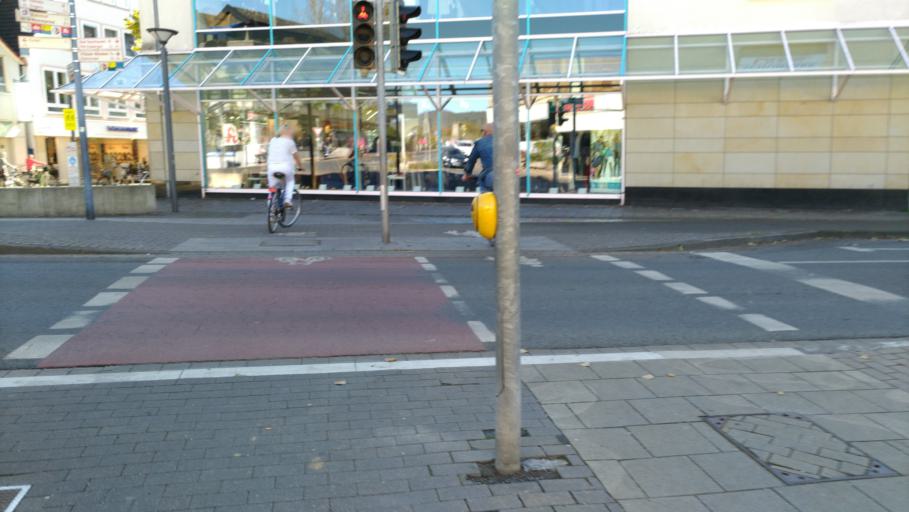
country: DE
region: Lower Saxony
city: Rinteln
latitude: 52.1893
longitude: 9.0807
